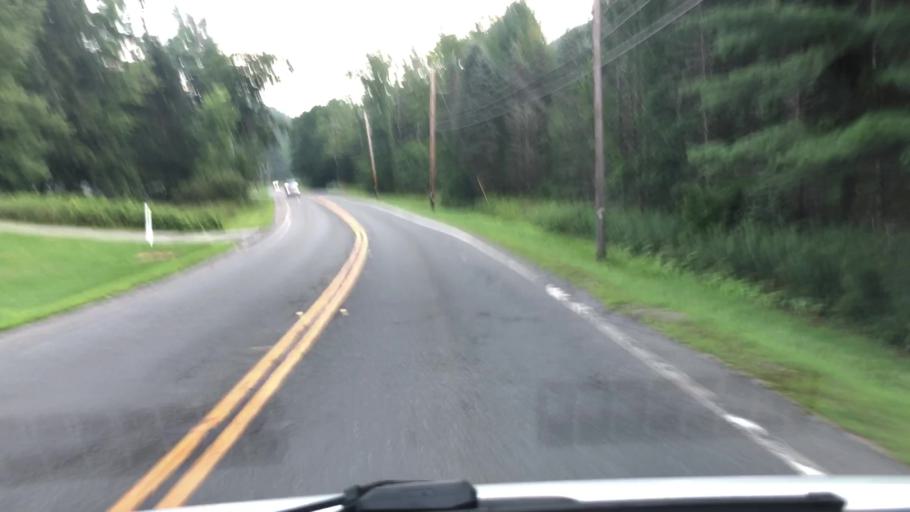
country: US
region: Massachusetts
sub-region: Berkshire County
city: Williamstown
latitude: 42.6961
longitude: -73.2258
